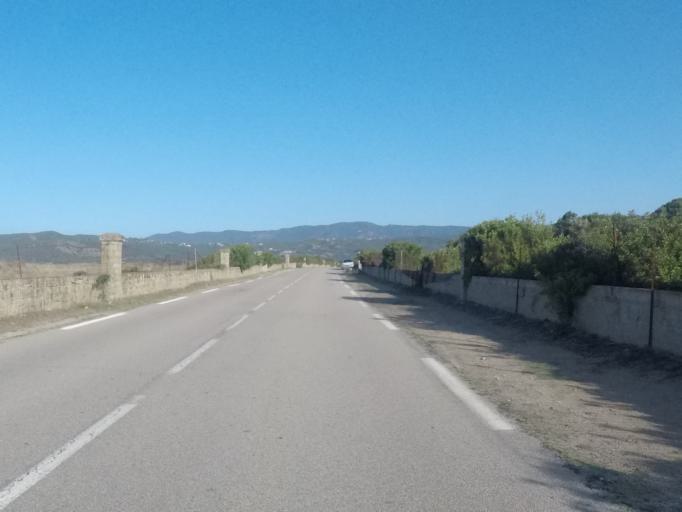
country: FR
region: Corsica
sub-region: Departement de la Corse-du-Sud
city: Propriano
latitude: 41.7048
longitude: 8.8334
